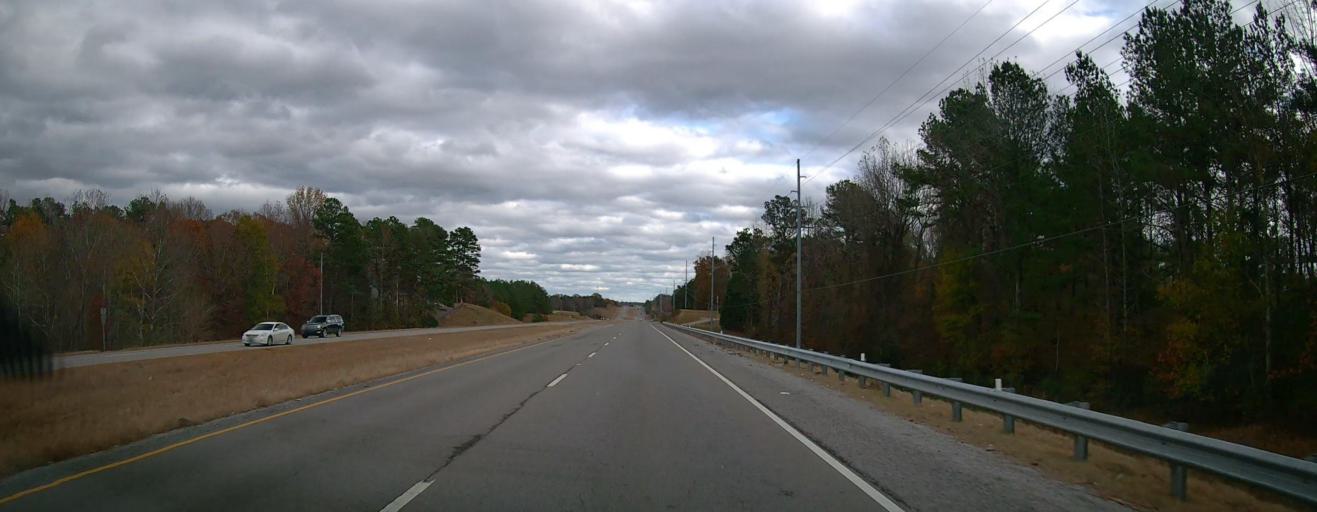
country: US
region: Alabama
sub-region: Lawrence County
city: Moulton
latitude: 34.5662
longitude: -87.3684
